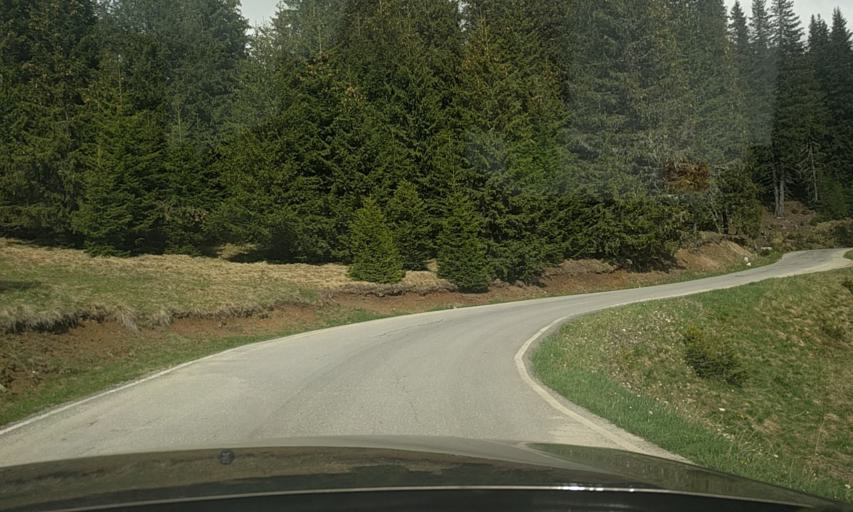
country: RO
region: Prahova
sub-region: Oras Busteni
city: Busteni
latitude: 45.3718
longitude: 25.4361
